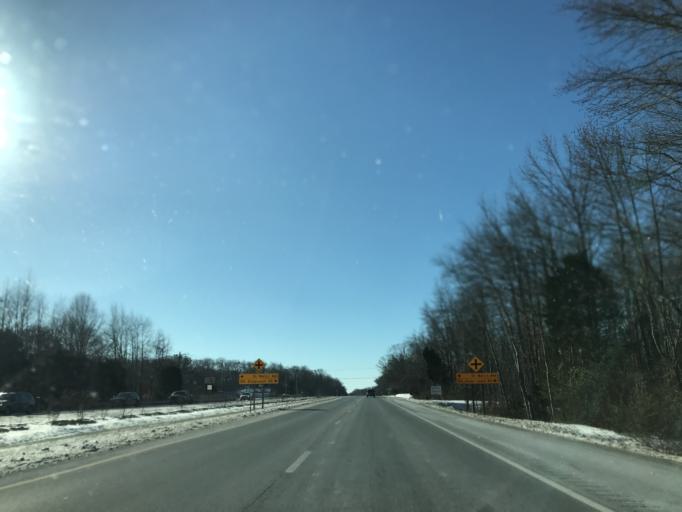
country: US
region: Maryland
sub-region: Charles County
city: La Plata
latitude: 38.5074
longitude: -76.9843
